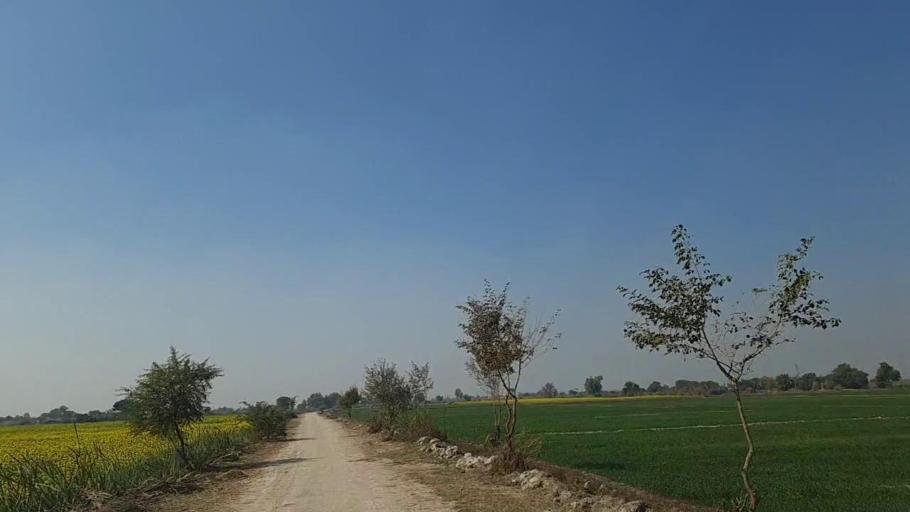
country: PK
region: Sindh
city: Daur
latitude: 26.5002
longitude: 68.3514
